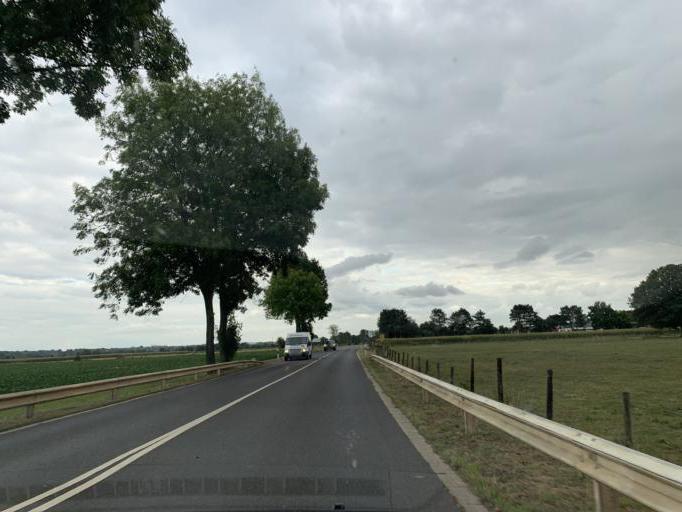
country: DE
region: North Rhine-Westphalia
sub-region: Regierungsbezirk Koln
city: Linnich
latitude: 51.0119
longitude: 6.2395
